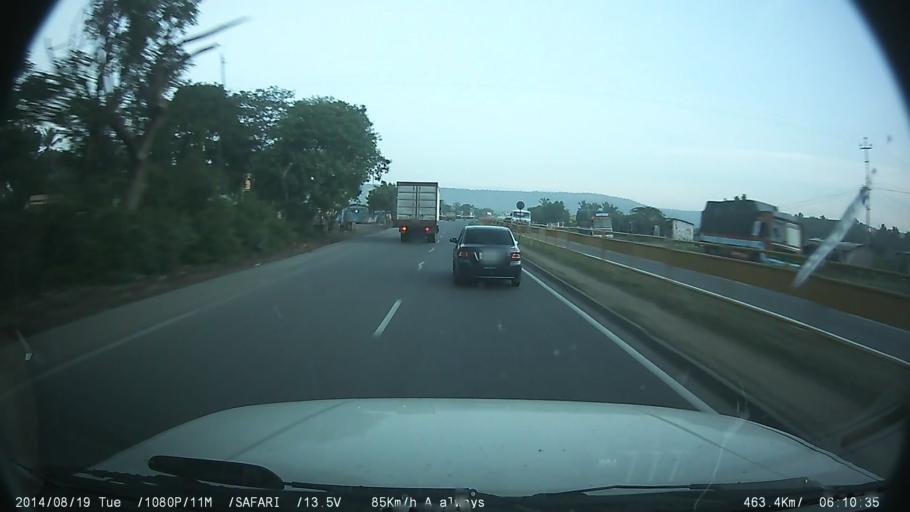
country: IN
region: Tamil Nadu
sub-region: Salem
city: Omalur
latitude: 11.9424
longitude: 78.0494
